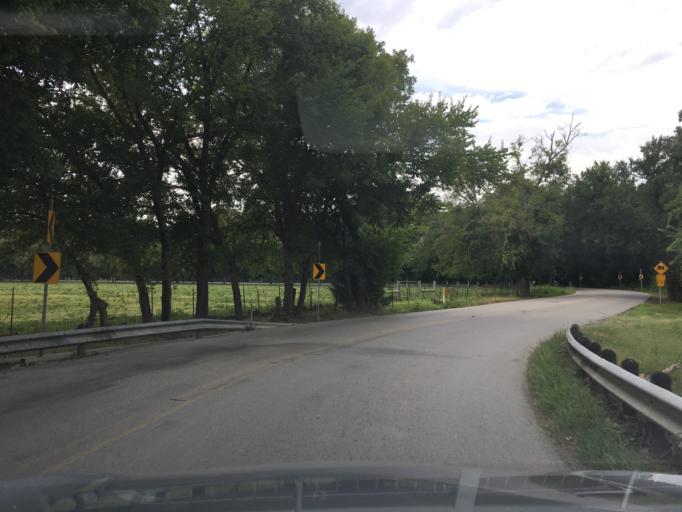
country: US
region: Texas
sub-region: Collin County
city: Saint Paul
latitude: 33.0325
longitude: -96.5810
